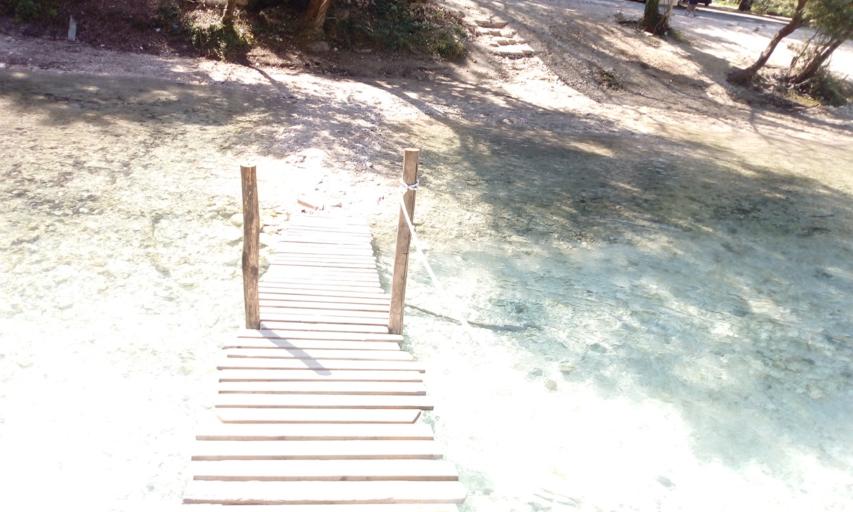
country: GR
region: Epirus
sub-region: Nomos Prevezis
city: Kanalaki
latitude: 39.3280
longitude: 20.6196
